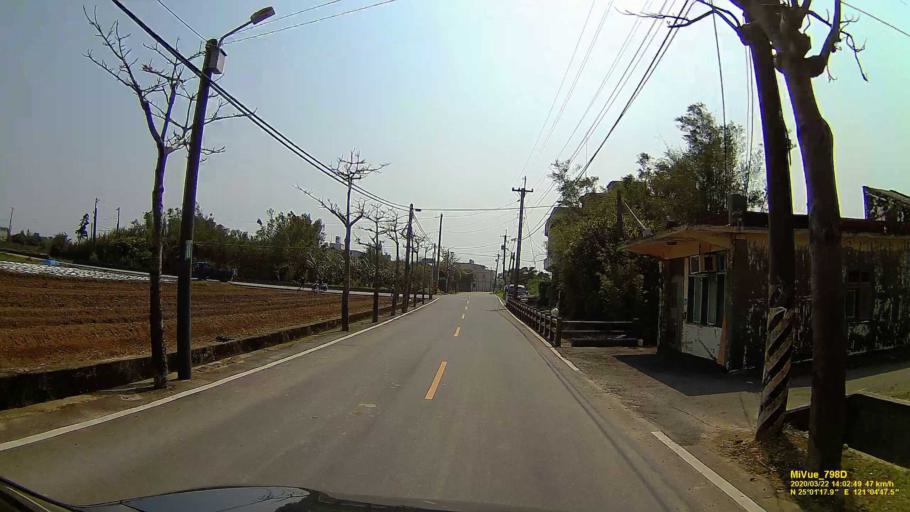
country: TW
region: Taiwan
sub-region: Hsinchu
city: Zhubei
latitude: 25.0210
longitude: 121.0792
